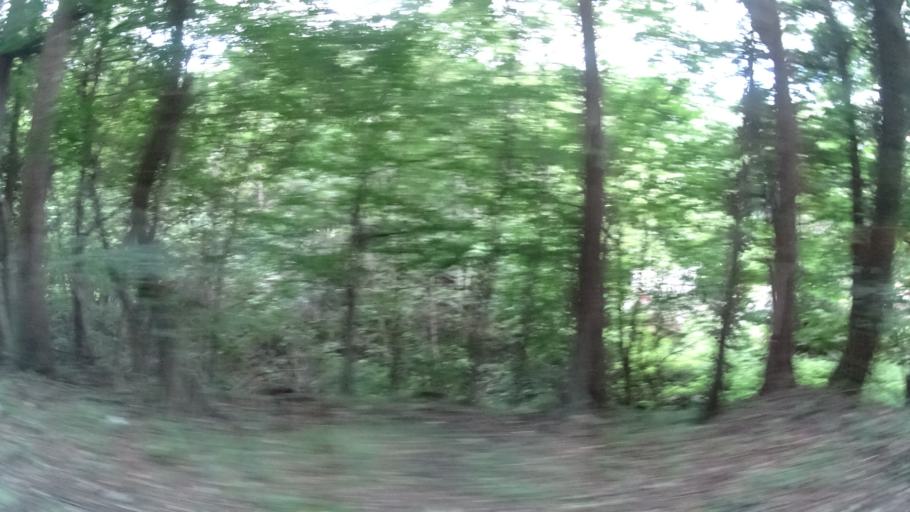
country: JP
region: Tochigi
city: Nikko
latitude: 36.6722
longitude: 139.4811
